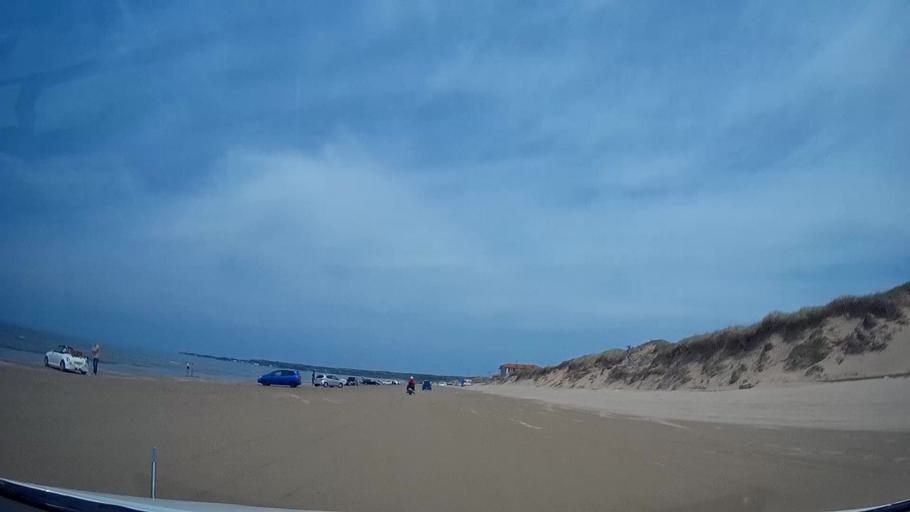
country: JP
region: Ishikawa
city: Hakui
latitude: 36.8903
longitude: 136.7651
